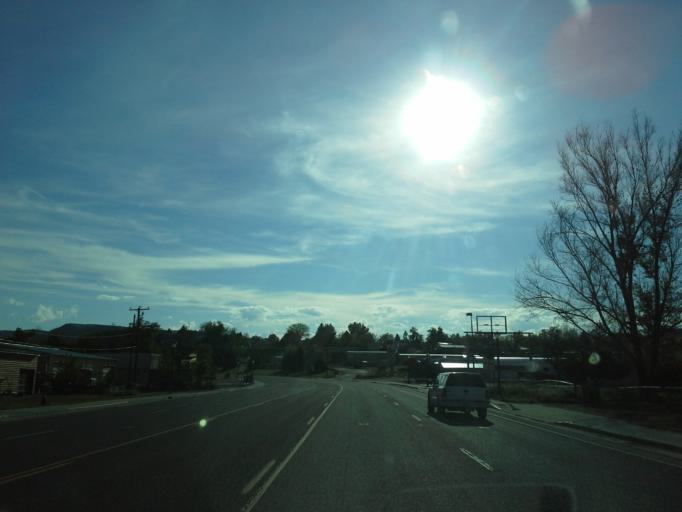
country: US
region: Wyoming
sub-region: Hot Springs County
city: Thermopolis
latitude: 43.6385
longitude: -108.2165
